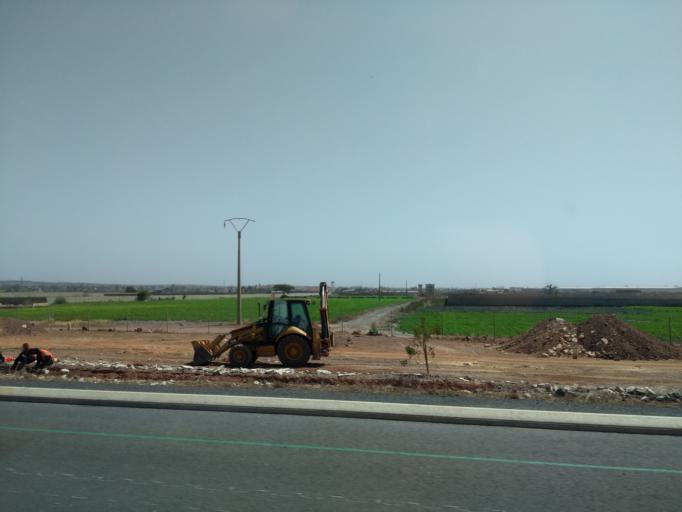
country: SN
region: Thies
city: Pout
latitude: 14.7348
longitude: -17.1645
